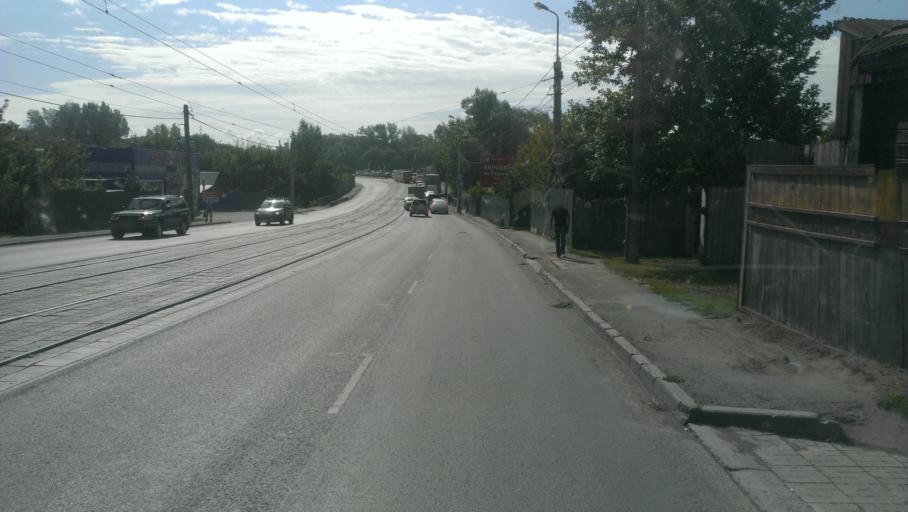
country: RU
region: Altai Krai
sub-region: Gorod Barnaulskiy
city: Barnaul
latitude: 53.3421
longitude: 83.7368
